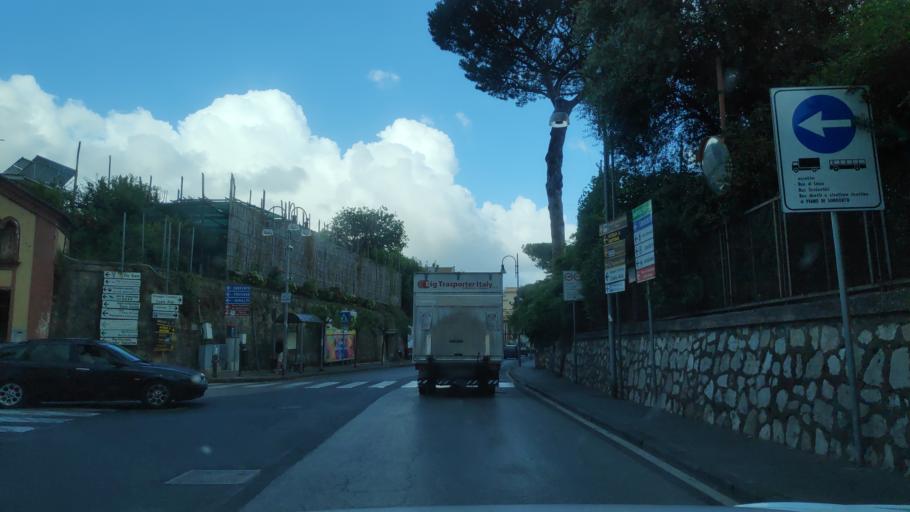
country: IT
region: Campania
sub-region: Provincia di Napoli
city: Meta
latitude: 40.6350
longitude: 14.4169
